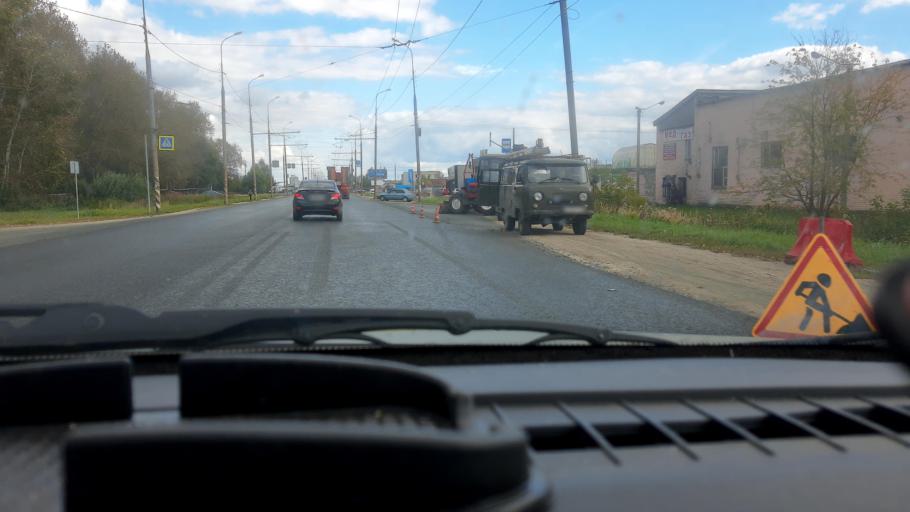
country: RU
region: Mariy-El
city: Medvedevo
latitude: 56.6379
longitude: 47.7710
